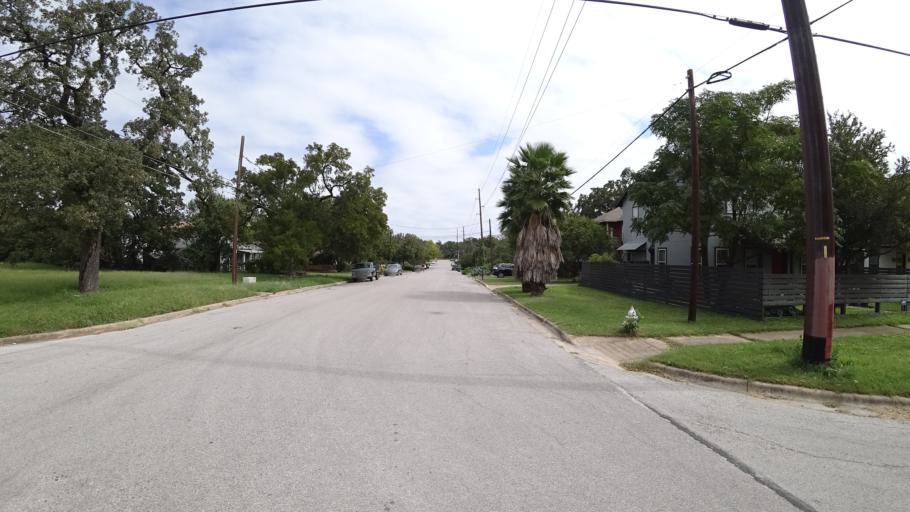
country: US
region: Texas
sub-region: Travis County
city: Austin
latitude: 30.2742
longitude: -97.7268
